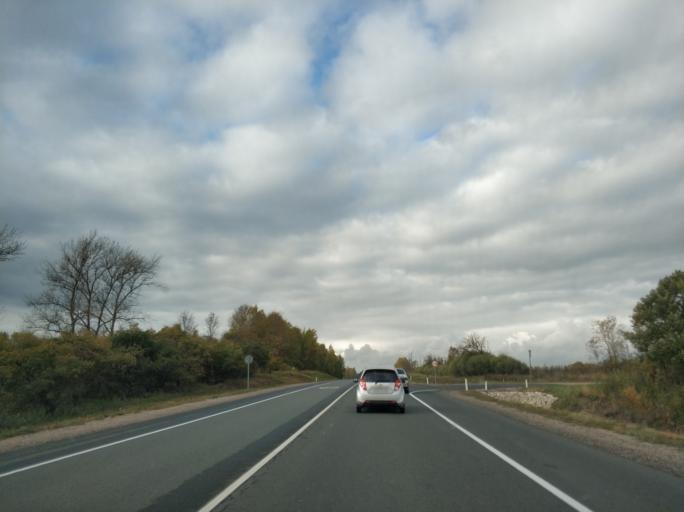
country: RU
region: Pskov
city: Ostrov
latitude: 57.4181
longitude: 28.3625
